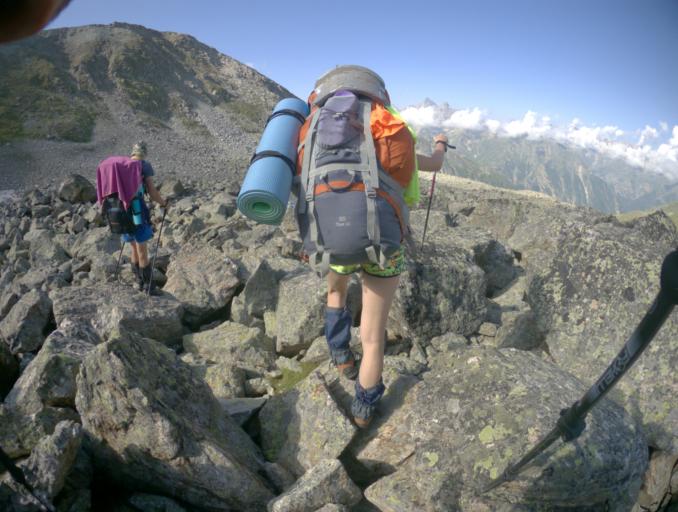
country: RU
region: Karachayevo-Cherkesiya
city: Uchkulan
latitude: 43.3091
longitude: 42.0662
